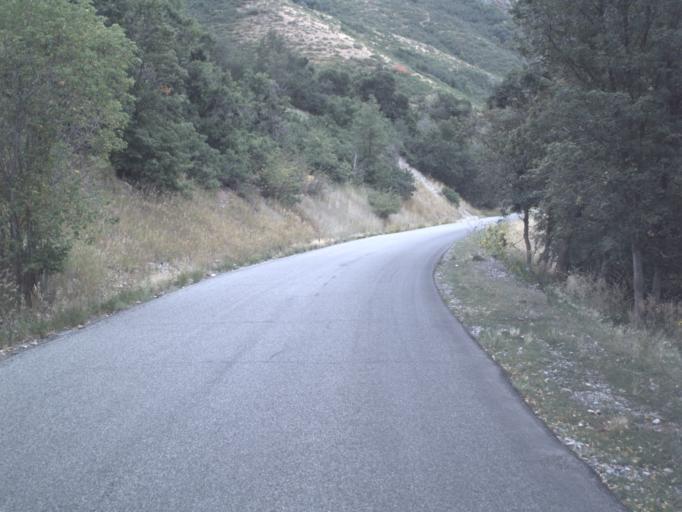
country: US
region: Utah
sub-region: Utah County
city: Lindon
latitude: 40.3954
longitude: -111.5842
